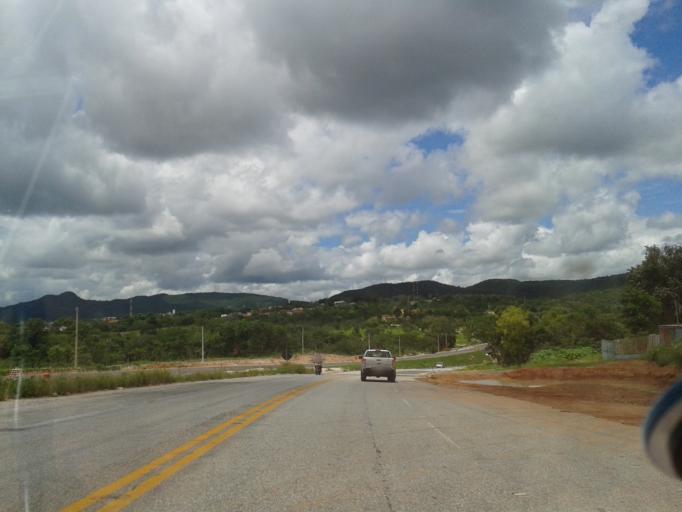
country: BR
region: Goias
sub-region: Goias
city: Goias
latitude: -15.9581
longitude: -50.1310
